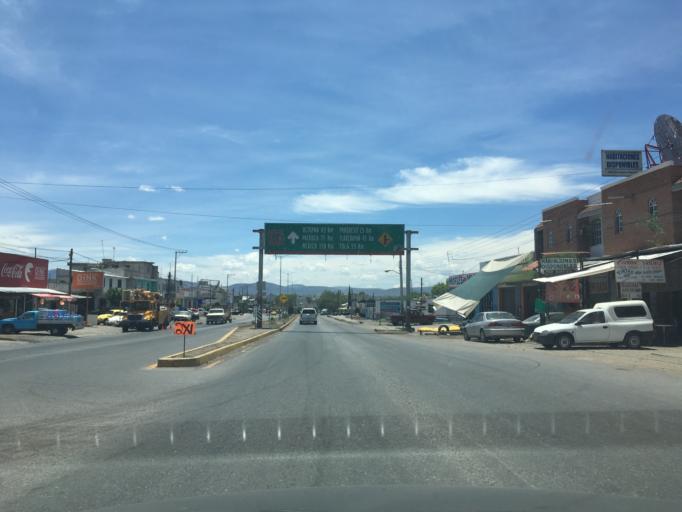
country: MX
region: Hidalgo
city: Ixmiquilpan
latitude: 20.4789
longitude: -99.2409
